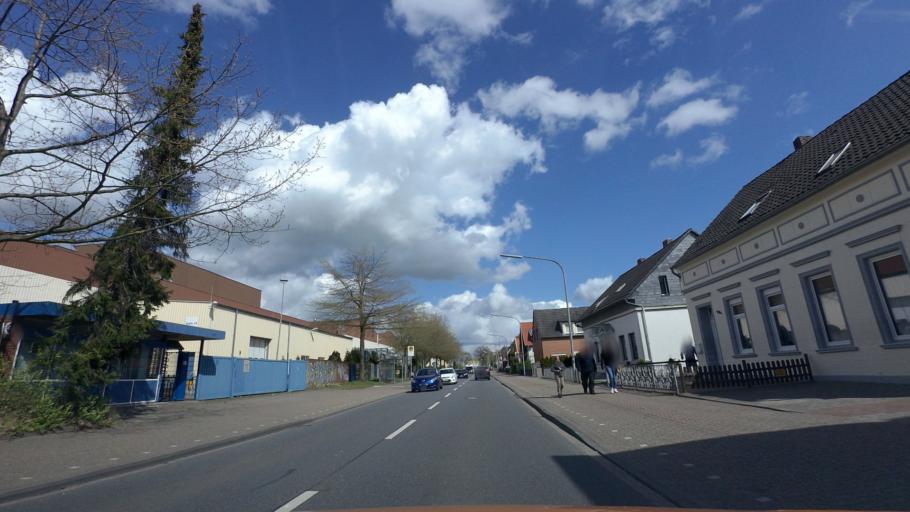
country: DE
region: Lower Saxony
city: Oldenburg
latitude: 53.1370
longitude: 8.2338
